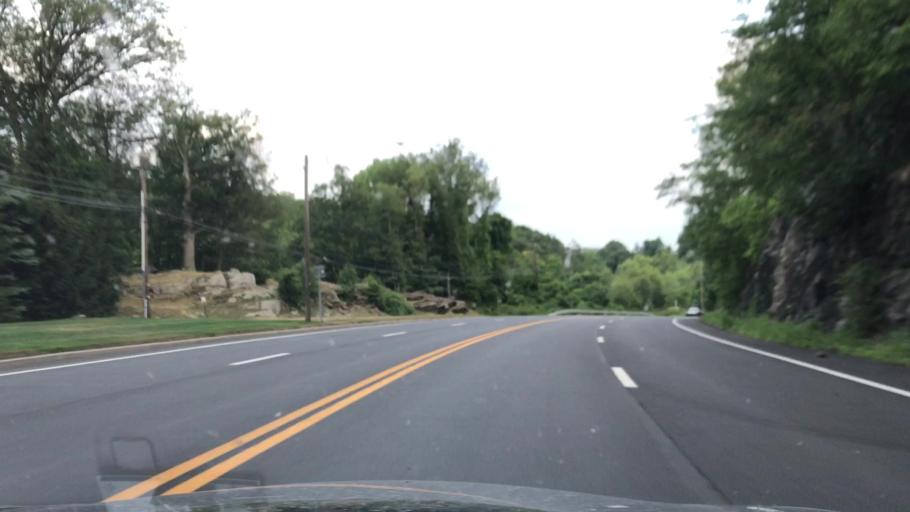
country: US
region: New York
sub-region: Rockland County
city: Sloatsburg
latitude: 41.2049
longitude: -74.1843
